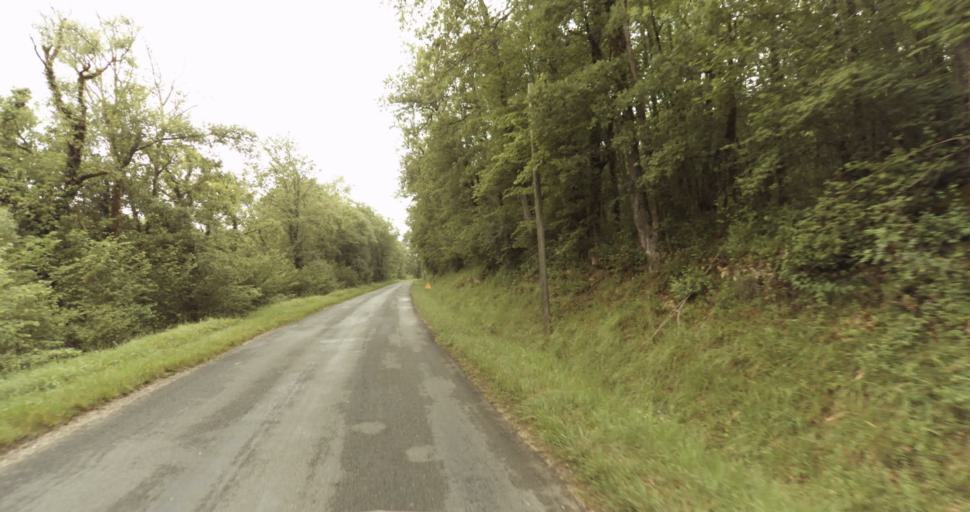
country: FR
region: Aquitaine
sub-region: Departement de la Dordogne
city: Lalinde
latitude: 44.8863
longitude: 0.7737
